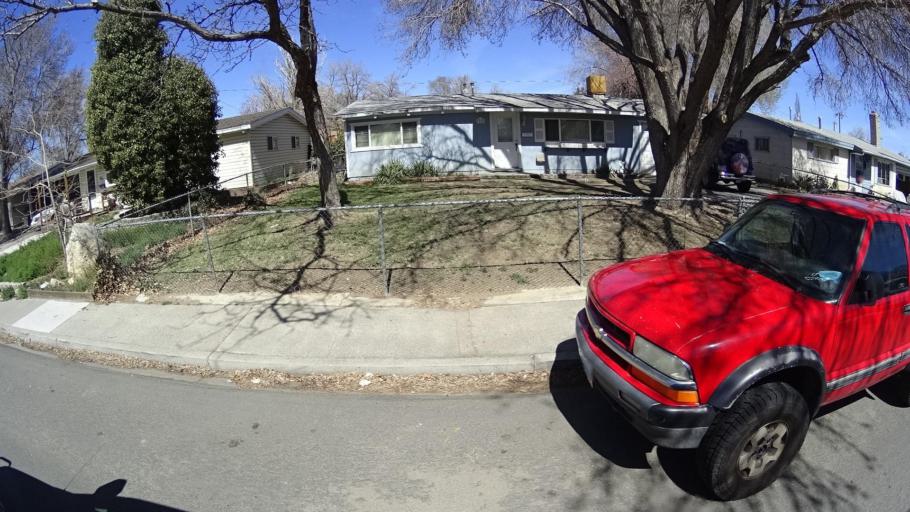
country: US
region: Nevada
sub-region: Washoe County
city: Sparks
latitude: 39.5474
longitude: -119.7550
